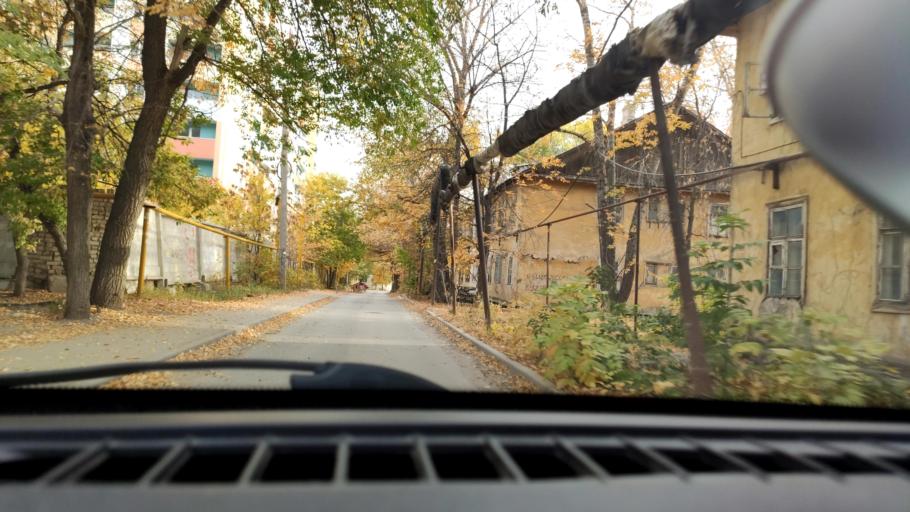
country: RU
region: Samara
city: Petra-Dubrava
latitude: 53.2771
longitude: 50.2673
